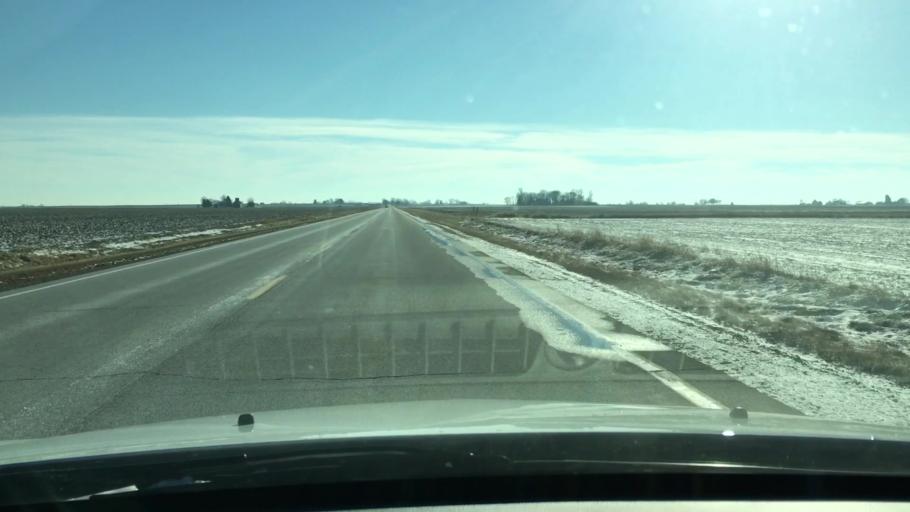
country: US
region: Illinois
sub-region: Ogle County
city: Rochelle
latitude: 41.8587
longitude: -89.0736
